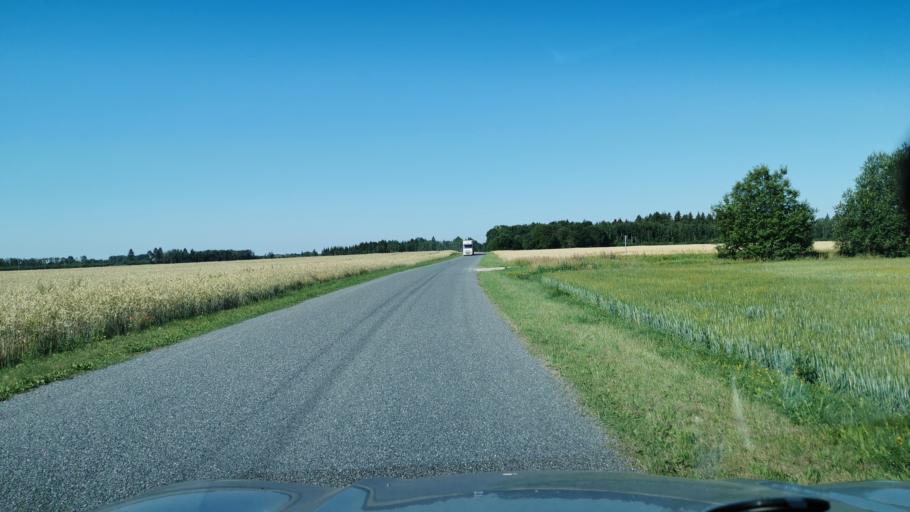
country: EE
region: Harju
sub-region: Paldiski linn
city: Paldiski
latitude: 59.2137
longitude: 24.0366
